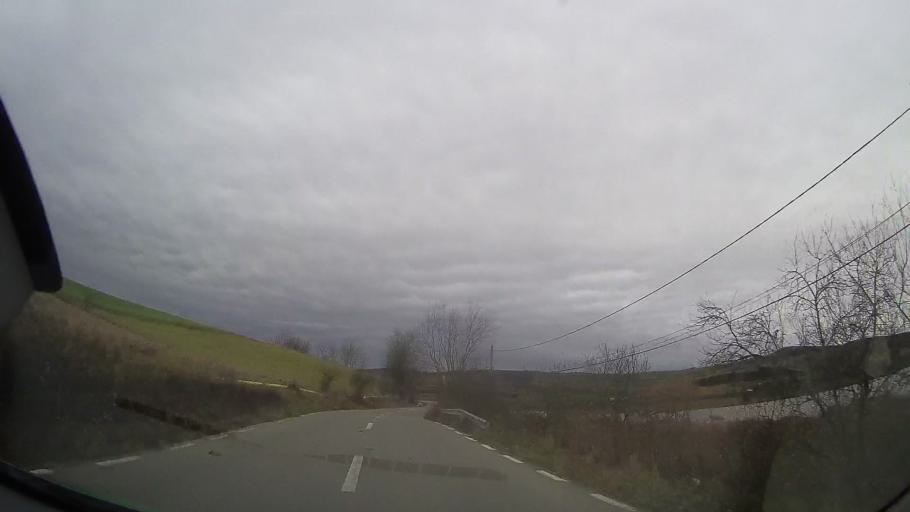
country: RO
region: Cluj
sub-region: Comuna Geaca
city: Geaca
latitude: 46.8399
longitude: 24.1353
